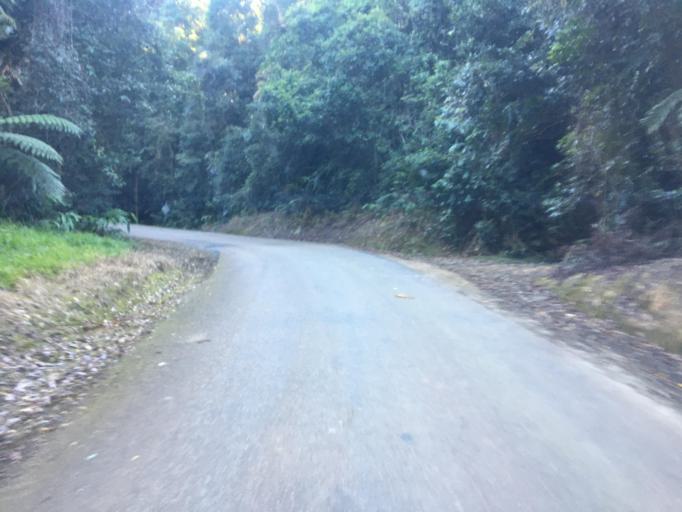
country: AU
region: Queensland
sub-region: Tablelands
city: Ravenshoe
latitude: -17.6104
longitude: 145.5601
